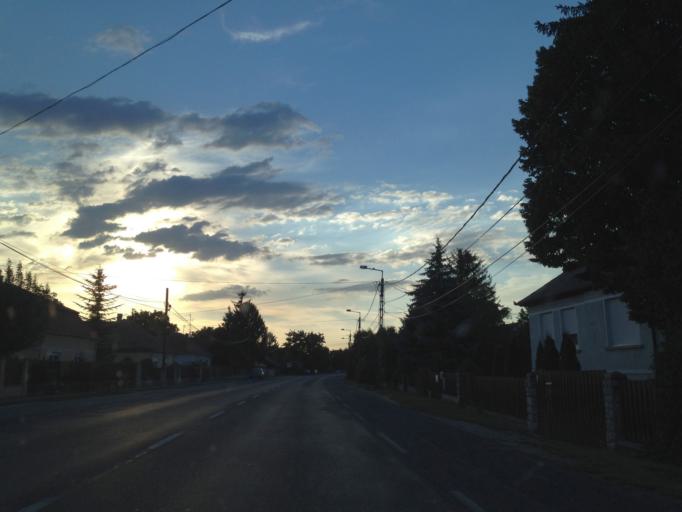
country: HU
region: Gyor-Moson-Sopron
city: Otteveny
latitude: 47.7295
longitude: 17.4848
